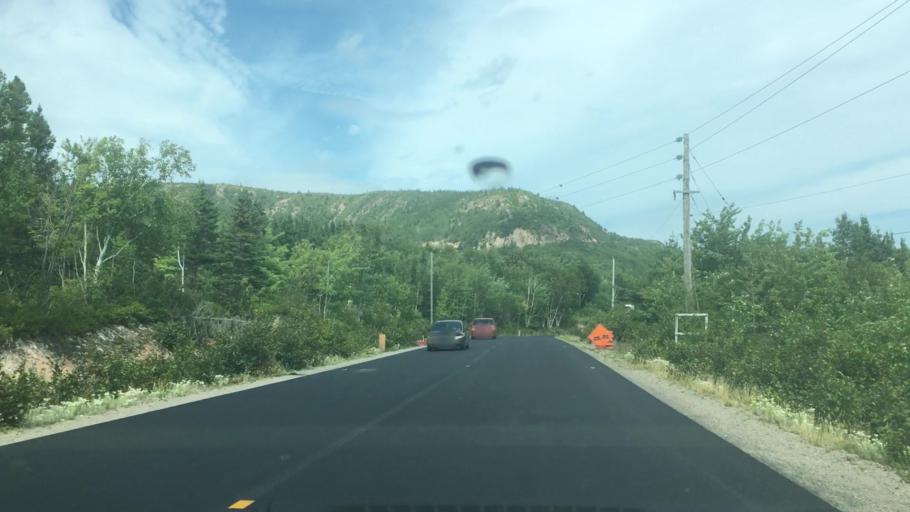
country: CA
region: Nova Scotia
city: Sydney Mines
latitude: 46.5747
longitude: -60.3916
